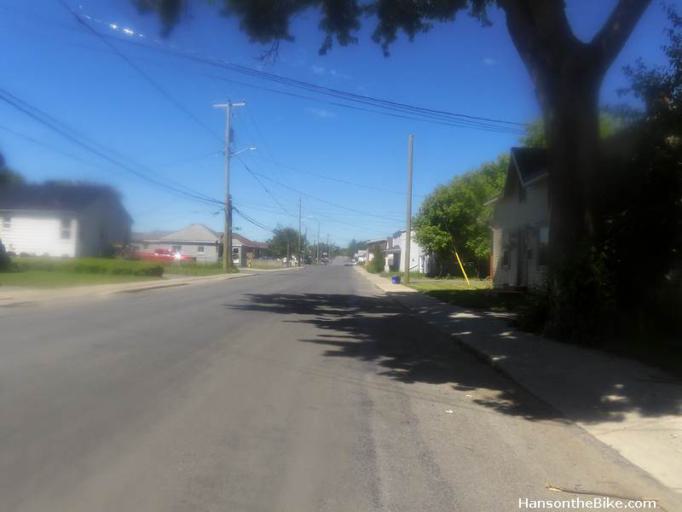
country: CA
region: Ontario
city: Kingston
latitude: 44.2530
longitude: -76.4858
